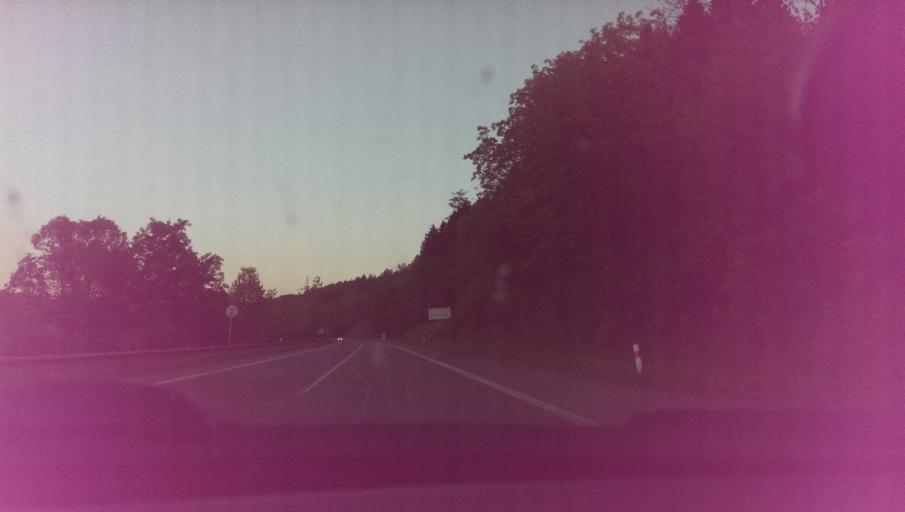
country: CZ
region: Zlin
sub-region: Okres Vsetin
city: Vsetin
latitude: 49.3410
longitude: 17.9747
